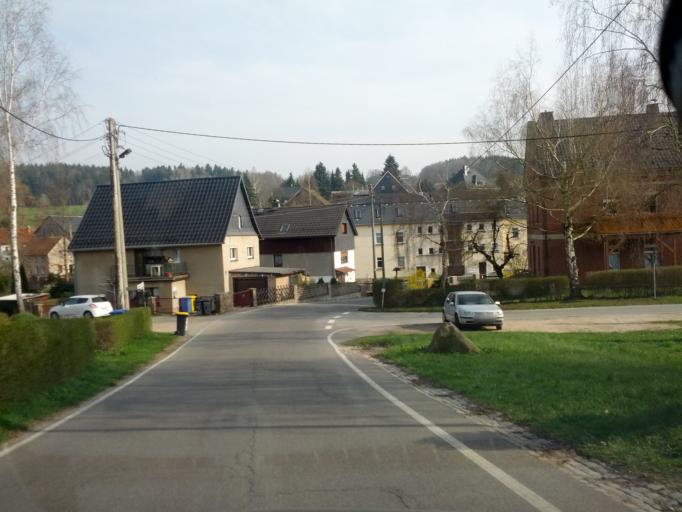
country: DE
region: Saxony
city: Stutzengrun
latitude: 50.5690
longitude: 12.5288
